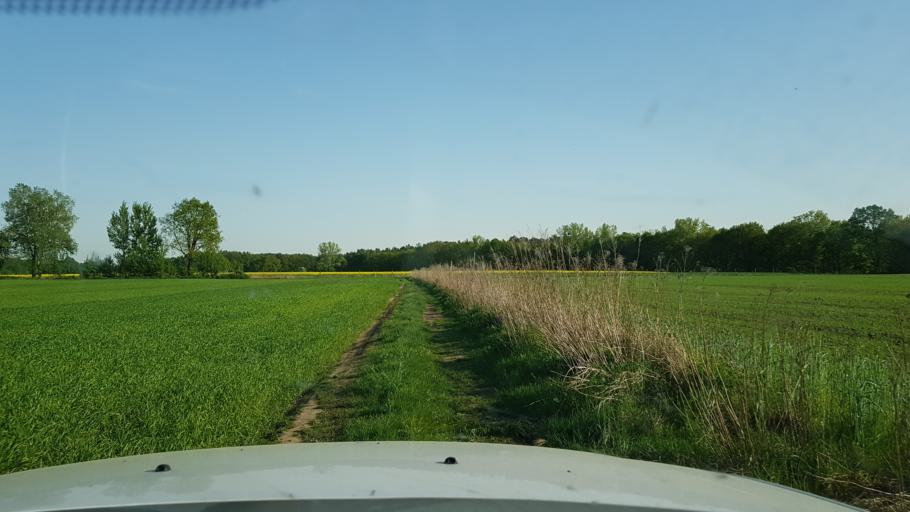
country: PL
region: West Pomeranian Voivodeship
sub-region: Powiat lobeski
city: Dobra
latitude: 53.6857
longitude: 15.3365
